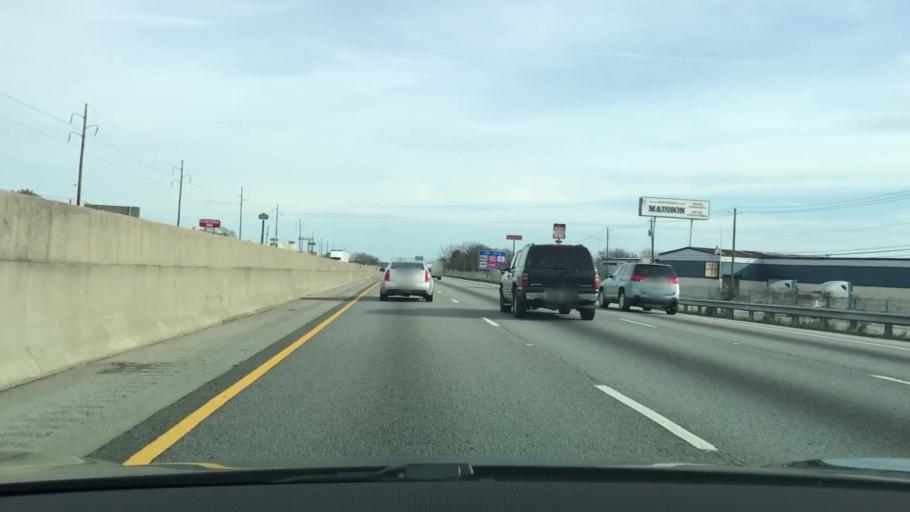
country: US
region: Georgia
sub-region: Rockdale County
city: Conyers
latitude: 33.6564
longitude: -84.0151
